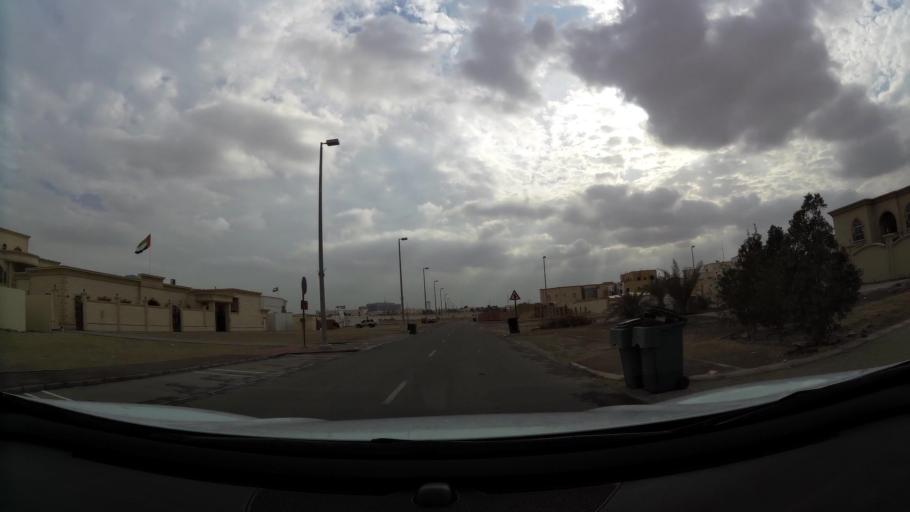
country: AE
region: Abu Dhabi
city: Abu Dhabi
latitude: 24.3407
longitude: 54.6218
